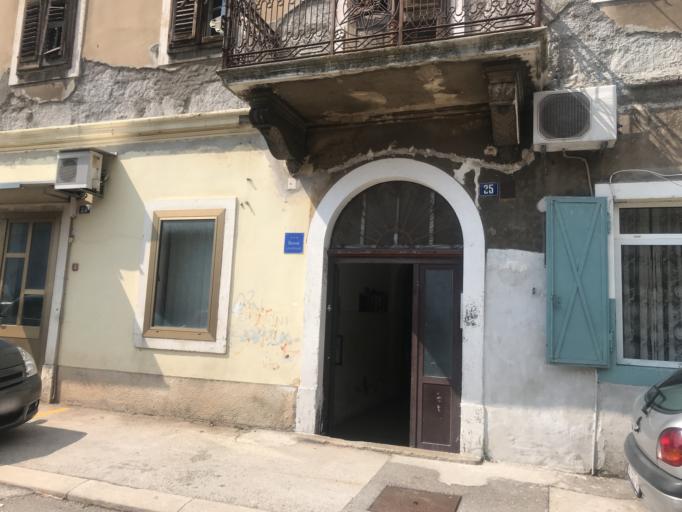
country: HR
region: Primorsko-Goranska
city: Drenova
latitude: 45.3314
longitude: 14.4510
